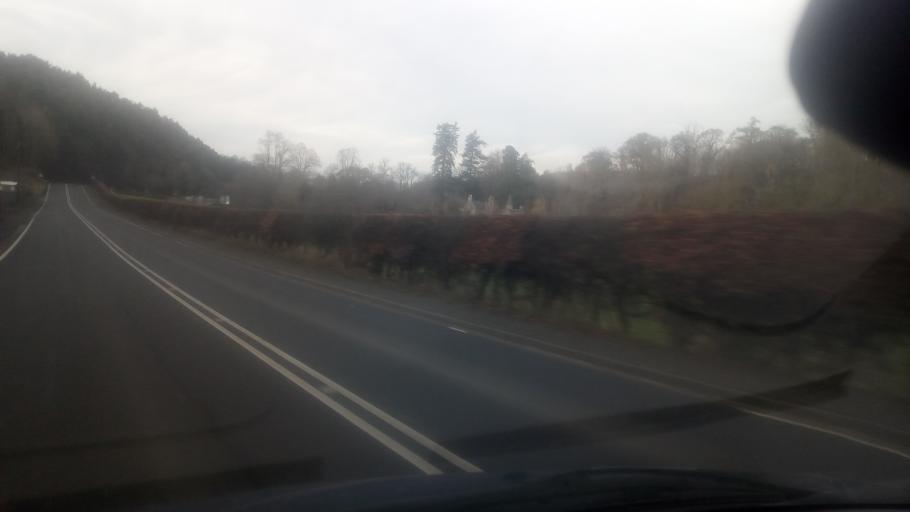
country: GB
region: Scotland
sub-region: The Scottish Borders
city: Jedburgh
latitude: 55.4652
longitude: -2.5532
